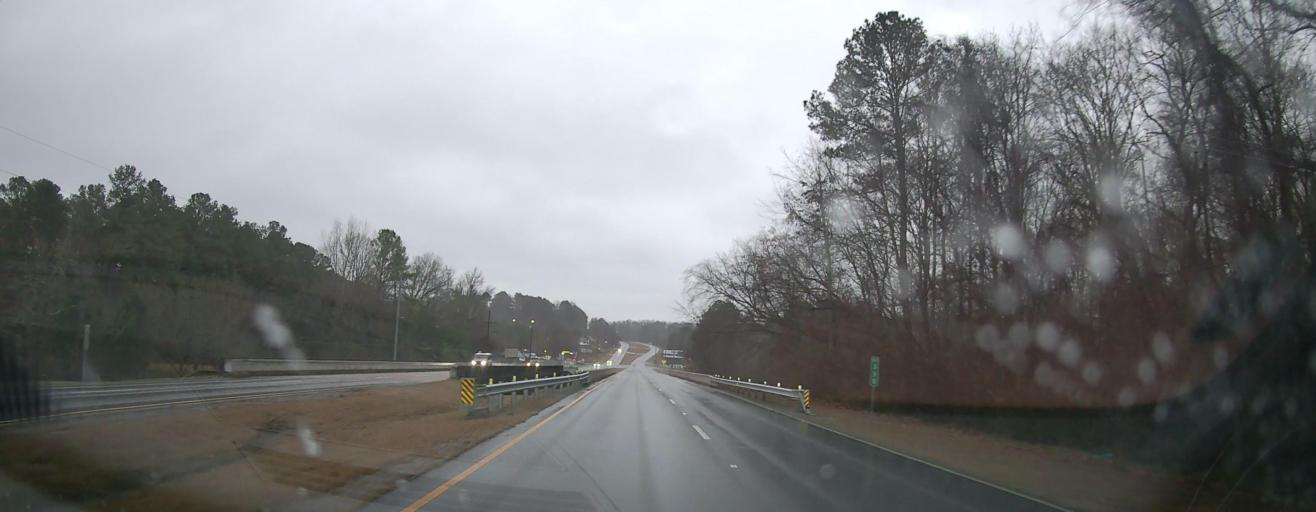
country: US
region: Alabama
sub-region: Morgan County
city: Flint City
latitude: 34.4922
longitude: -86.9654
